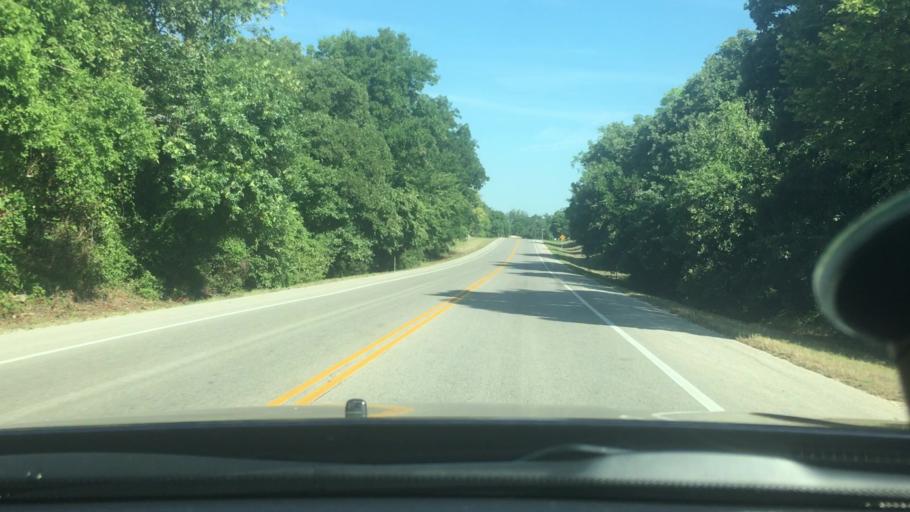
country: US
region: Oklahoma
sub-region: Garvin County
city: Wynnewood
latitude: 34.6817
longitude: -97.2100
